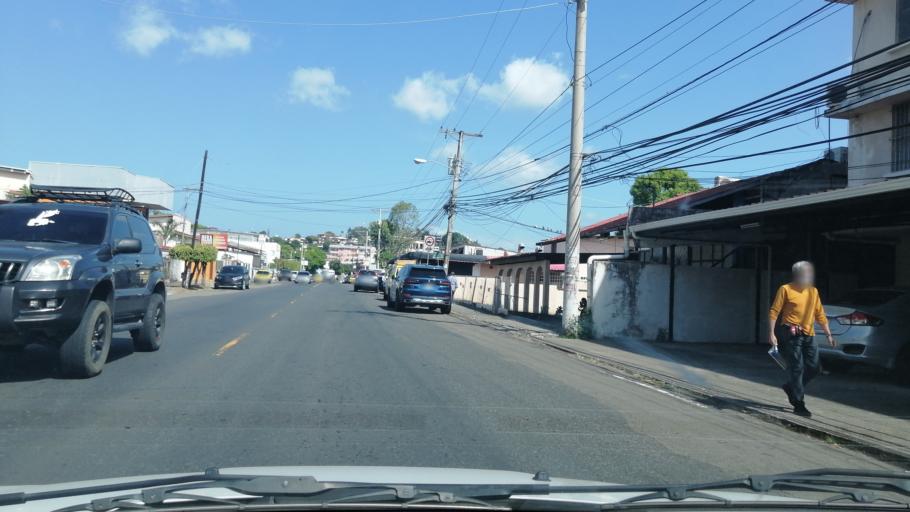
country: PA
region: Panama
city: Panama
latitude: 9.0074
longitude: -79.5232
